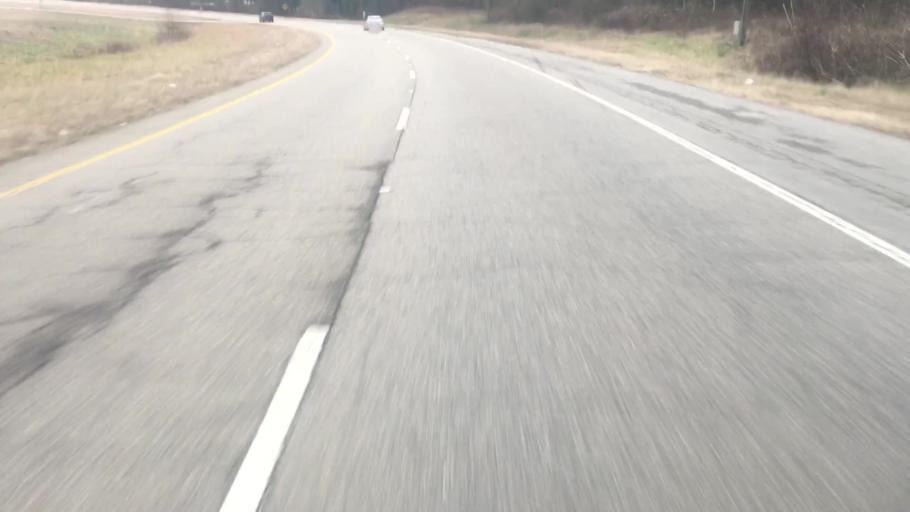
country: US
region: Alabama
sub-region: Walker County
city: Cordova
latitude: 33.8094
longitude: -87.1470
